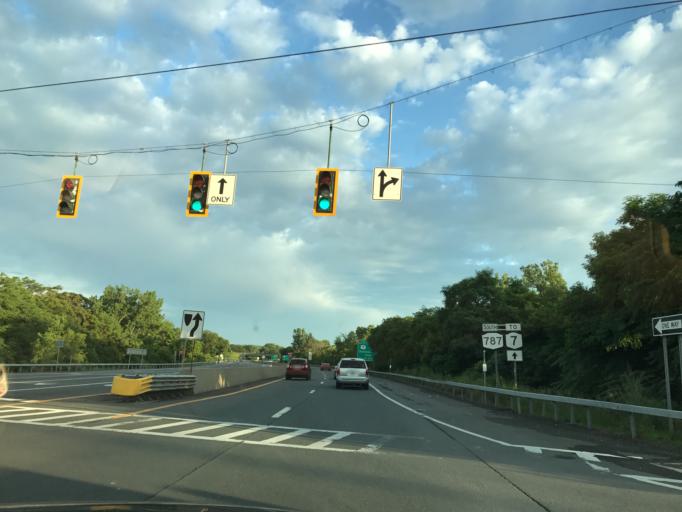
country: US
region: New York
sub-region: Albany County
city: Green Island
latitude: 42.7500
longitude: -73.6993
